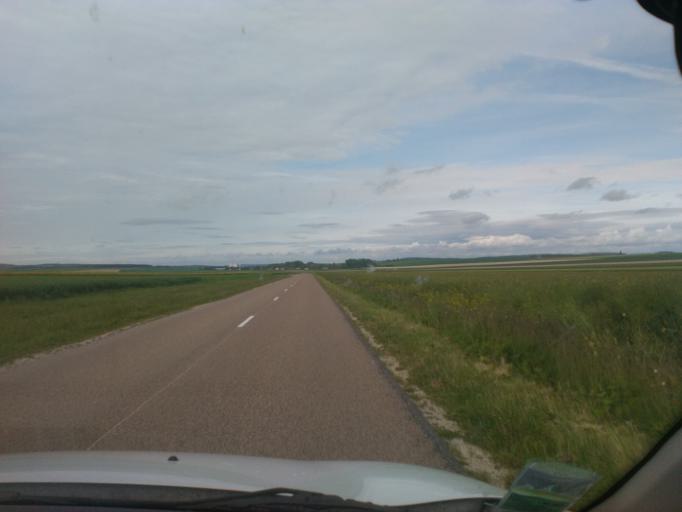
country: FR
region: Champagne-Ardenne
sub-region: Departement de l'Aube
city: Marigny-le-Chatel
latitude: 48.3620
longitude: 3.7397
